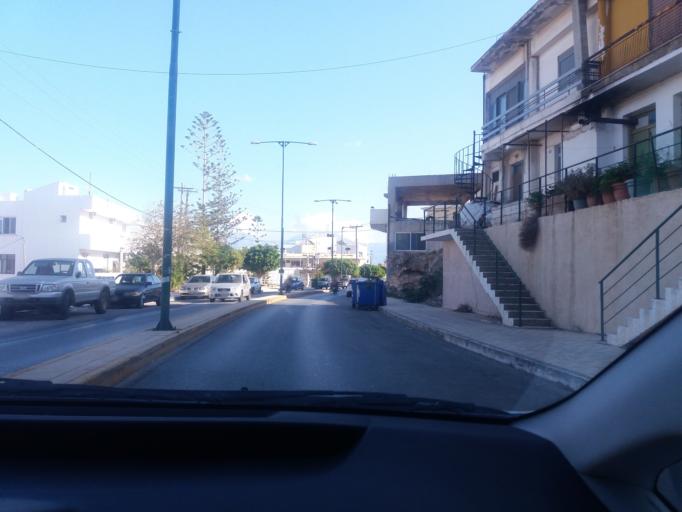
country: GR
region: Crete
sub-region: Nomos Lasithiou
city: Agios Nikolaos
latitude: 35.1961
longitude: 25.7122
